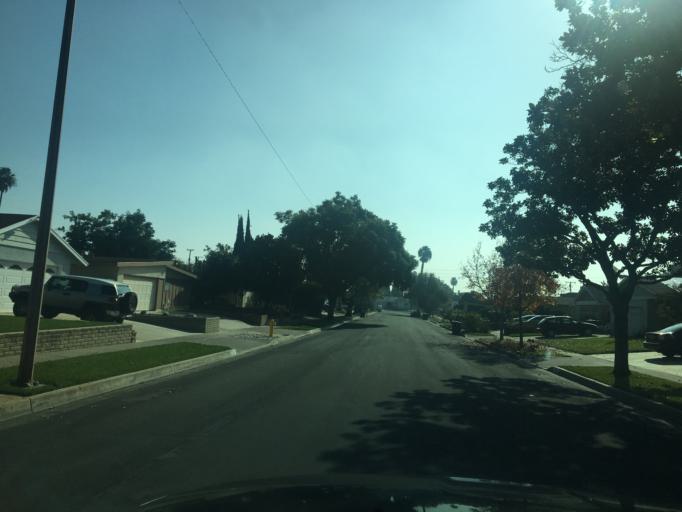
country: US
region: California
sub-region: Orange County
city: Tustin
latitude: 33.7362
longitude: -117.8297
